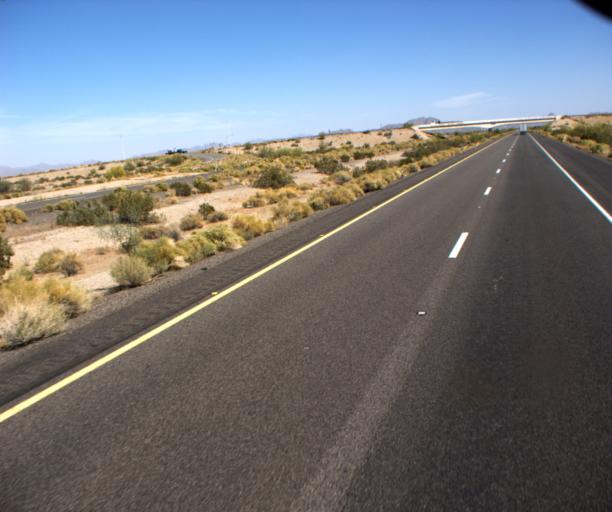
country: US
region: Arizona
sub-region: Maricopa County
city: Gila Bend
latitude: 32.9260
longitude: -112.6752
